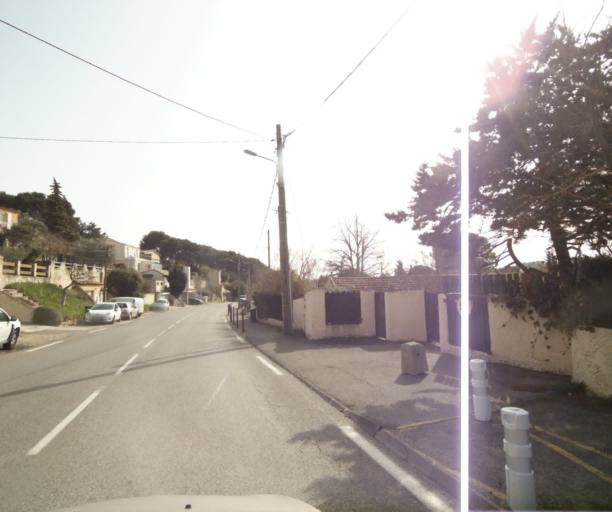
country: FR
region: Provence-Alpes-Cote d'Azur
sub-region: Departement des Bouches-du-Rhone
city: Septemes-les-Vallons
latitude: 43.3943
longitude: 5.3439
